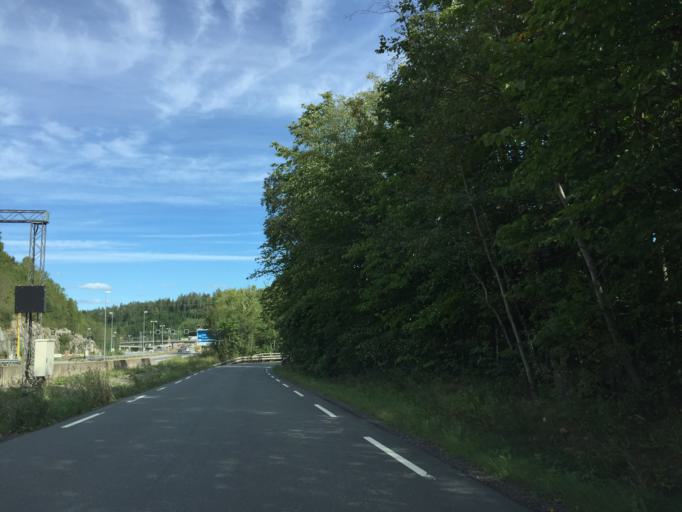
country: NO
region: Akershus
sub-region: As
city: As
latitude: 59.7032
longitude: 10.7380
